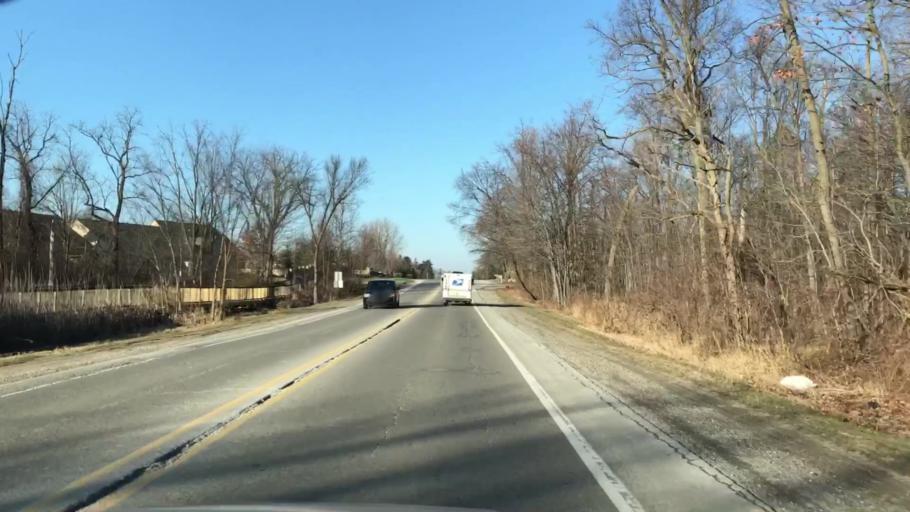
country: US
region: Michigan
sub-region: Oakland County
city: Novi
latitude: 42.4728
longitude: -83.5146
